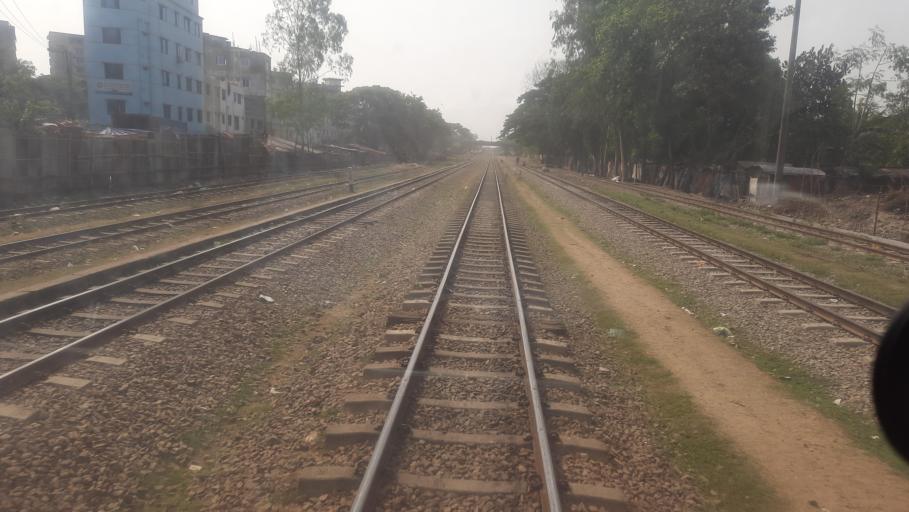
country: BD
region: Chittagong
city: Chittagong
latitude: 22.3386
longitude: 91.8175
